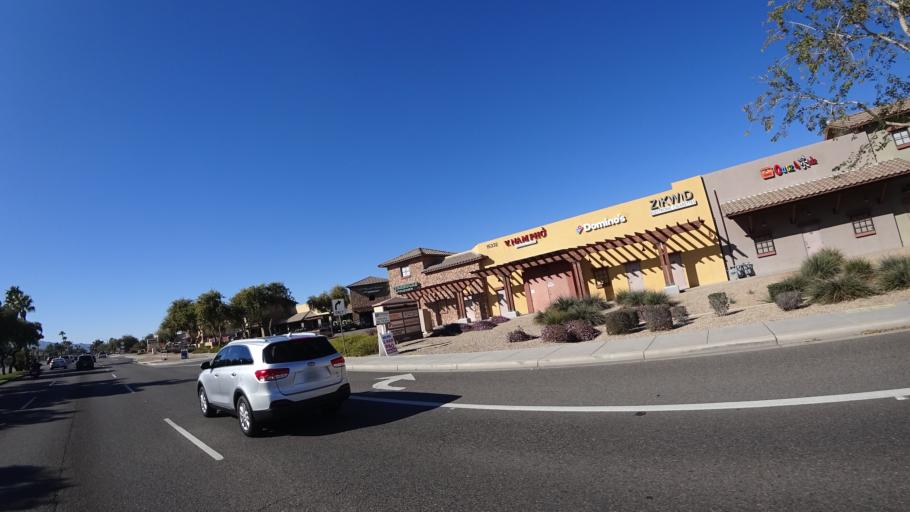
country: US
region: Arizona
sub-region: Maricopa County
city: Sun City West
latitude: 33.6388
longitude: -112.3905
